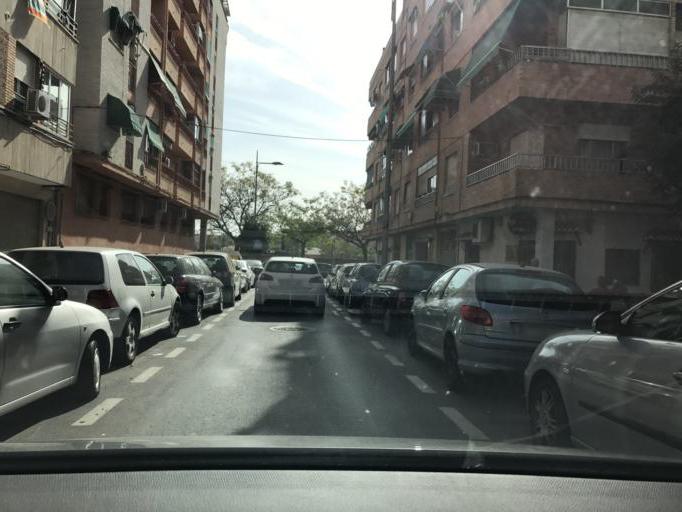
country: ES
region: Andalusia
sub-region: Provincia de Granada
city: Granada
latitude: 37.1854
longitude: -3.6112
